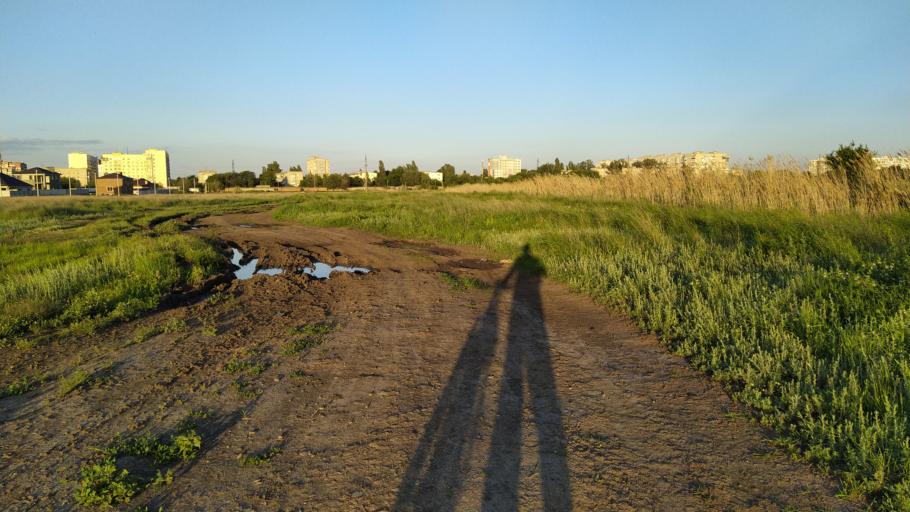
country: RU
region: Rostov
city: Bataysk
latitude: 47.1268
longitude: 39.7254
